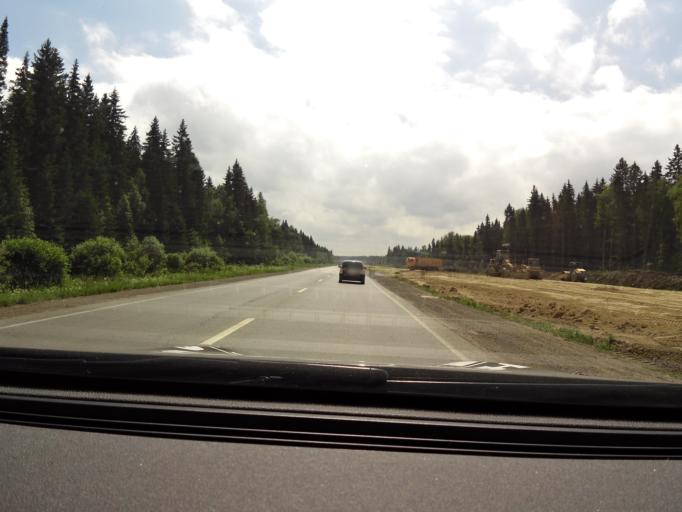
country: RU
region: Perm
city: Kukushtan
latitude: 57.6584
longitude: 56.4409
